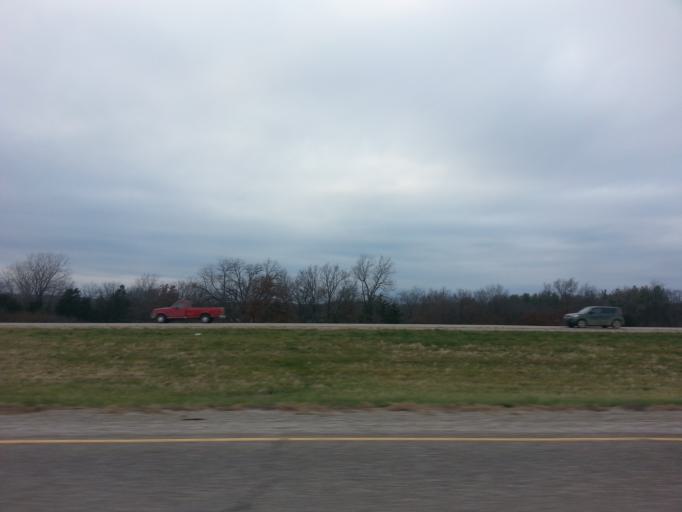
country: US
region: Iowa
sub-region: Henry County
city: Mount Pleasant
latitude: 40.9040
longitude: -91.5510
